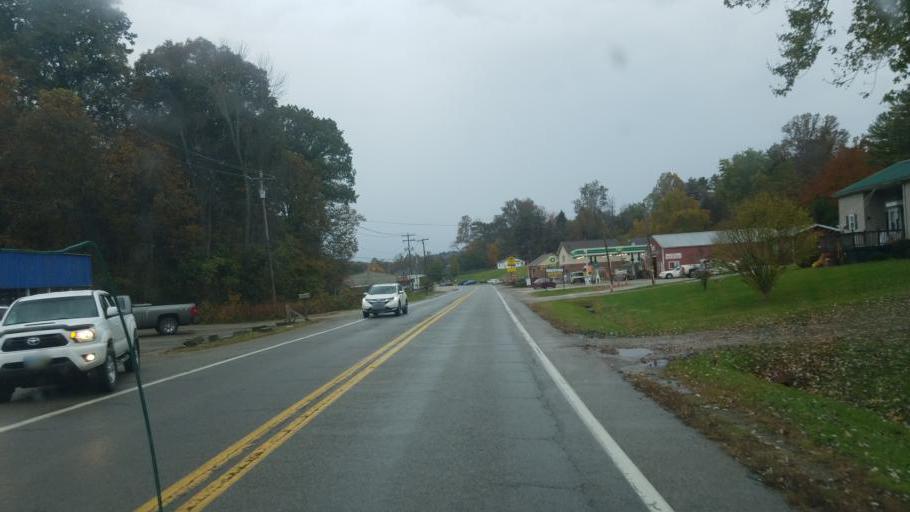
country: US
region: West Virginia
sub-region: Wood County
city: Boaz
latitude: 39.3457
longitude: -81.5256
